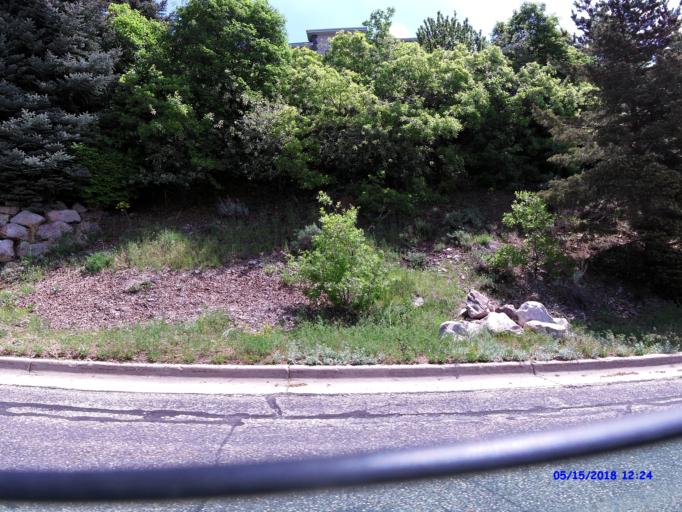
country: US
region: Utah
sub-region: Weber County
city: Uintah
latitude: 41.1705
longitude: -111.9239
